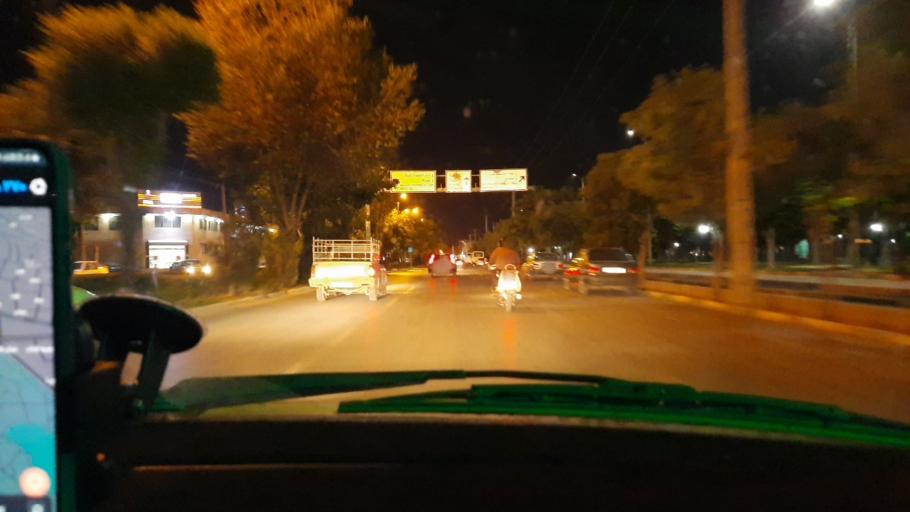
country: IR
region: Markazi
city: Arak
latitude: 34.1072
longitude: 49.6970
